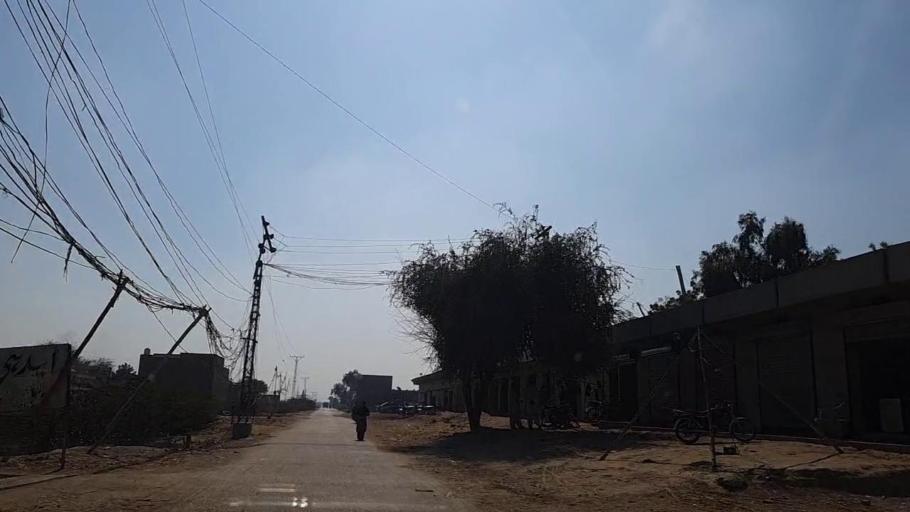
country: PK
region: Sindh
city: Sakrand
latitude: 26.2972
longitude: 68.1080
